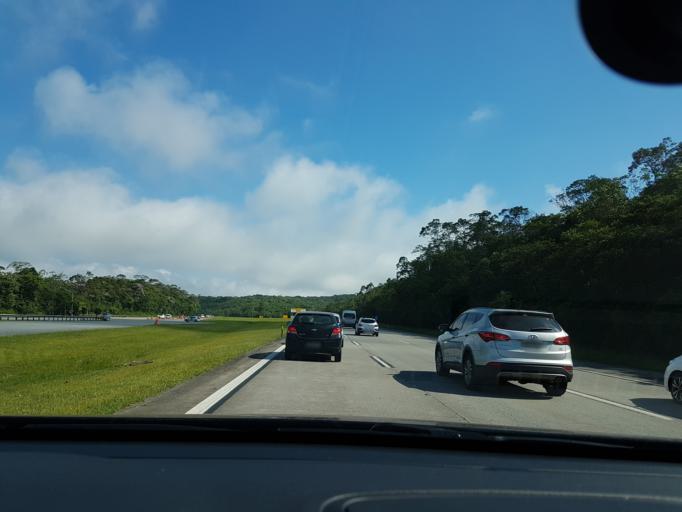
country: BR
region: Sao Paulo
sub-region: Cubatao
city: Cubatao
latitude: -23.9210
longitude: -46.5556
